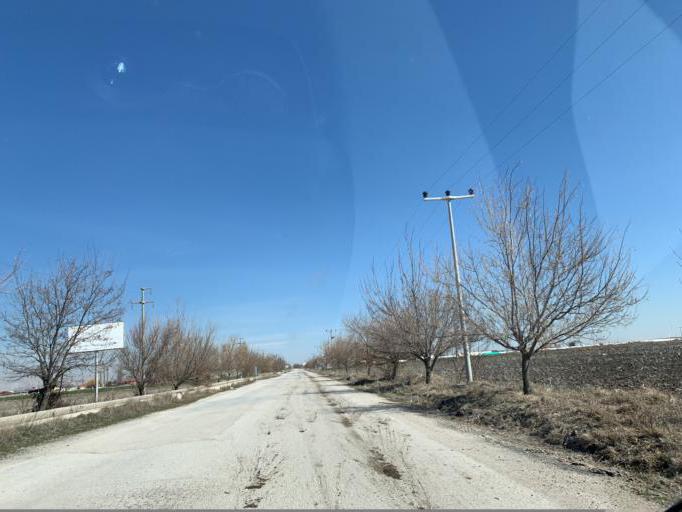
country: TR
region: Konya
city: Catalhoeyuek
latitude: 37.7478
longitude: 32.8344
